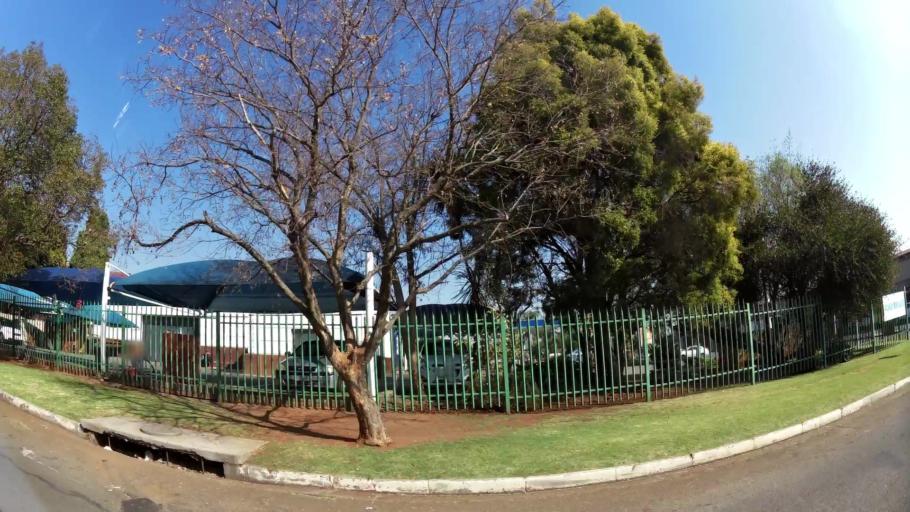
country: ZA
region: Gauteng
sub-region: Ekurhuleni Metropolitan Municipality
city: Boksburg
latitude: -26.2459
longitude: 28.2647
